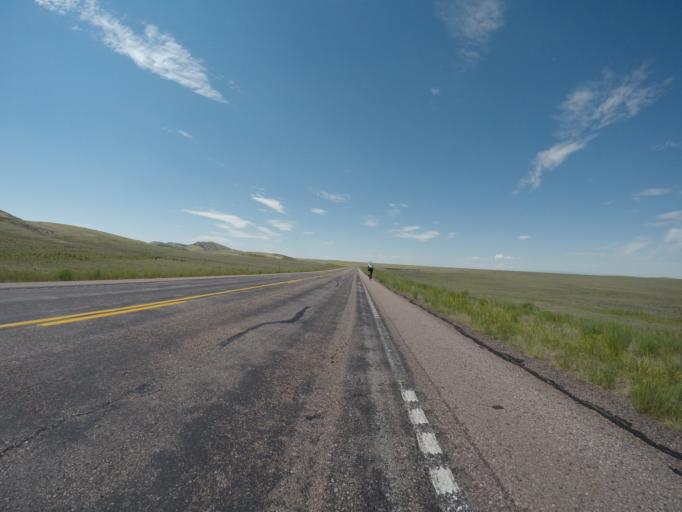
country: US
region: Wyoming
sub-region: Albany County
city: Laramie
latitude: 41.6755
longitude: -105.5286
